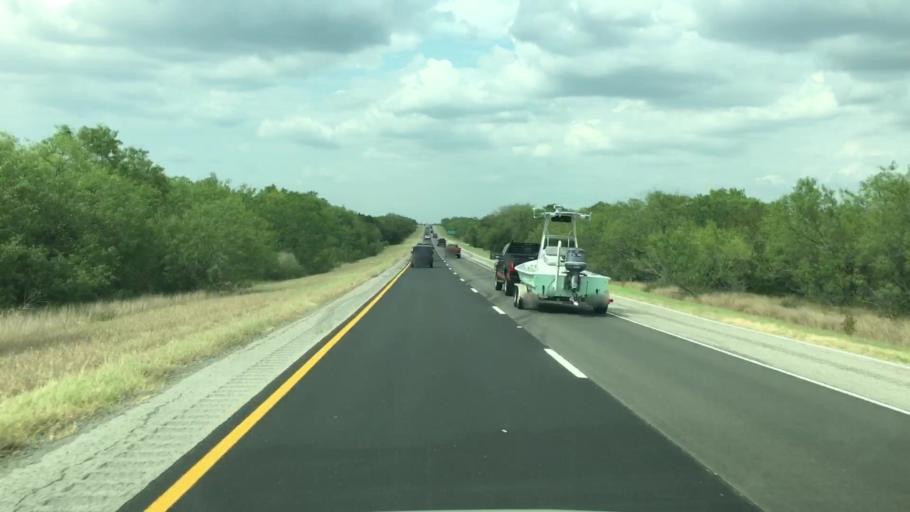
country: US
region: Texas
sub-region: Atascosa County
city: Pleasanton
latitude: 28.9285
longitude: -98.4351
